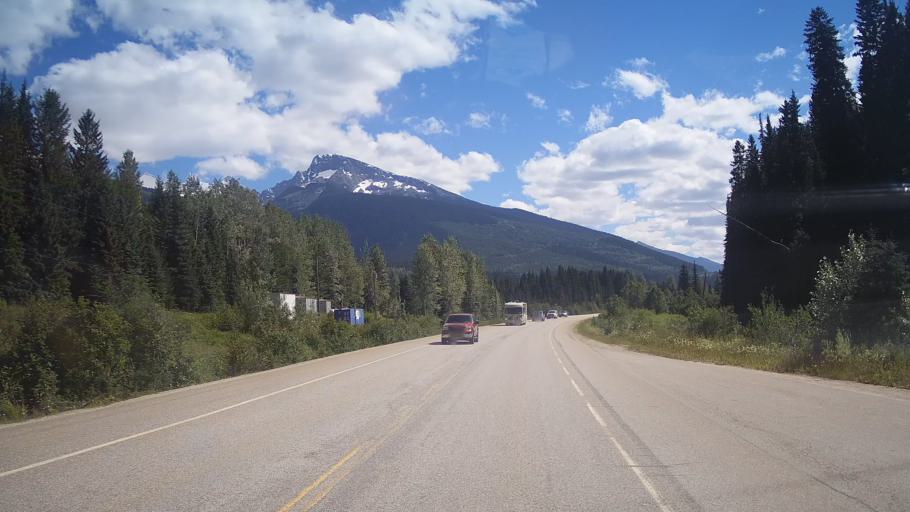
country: CA
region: Alberta
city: Jasper Park Lodge
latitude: 52.5855
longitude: -119.0953
